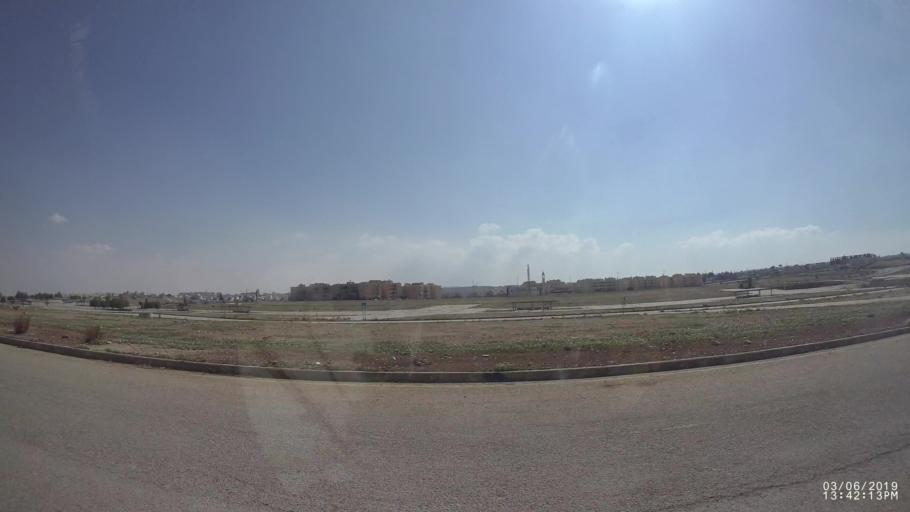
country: JO
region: Zarqa
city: Zarqa
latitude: 32.0709
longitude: 36.1098
